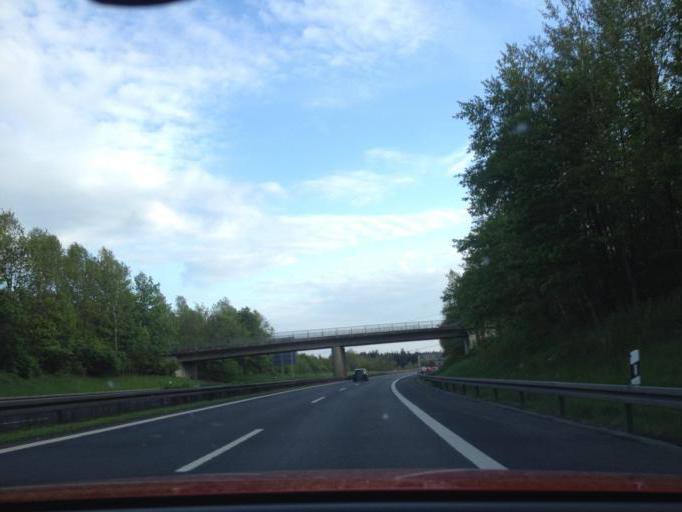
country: DE
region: Bavaria
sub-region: Upper Palatinate
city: Mitterteich
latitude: 49.9283
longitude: 12.2262
